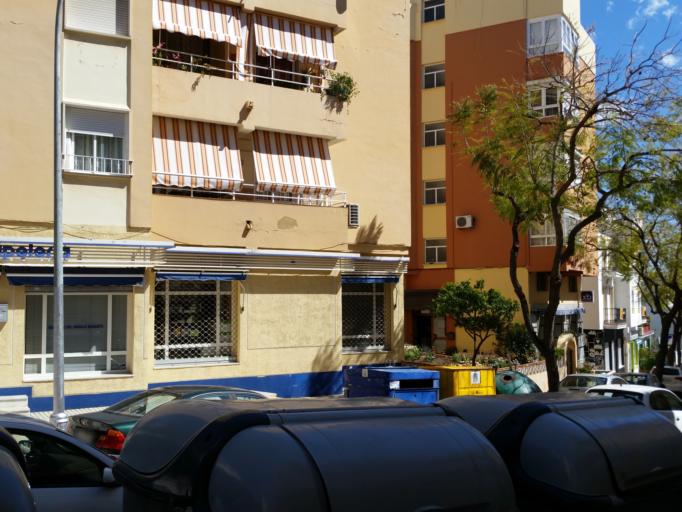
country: ES
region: Andalusia
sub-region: Provincia de Malaga
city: Benalmadena
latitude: 36.6013
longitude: -4.5332
